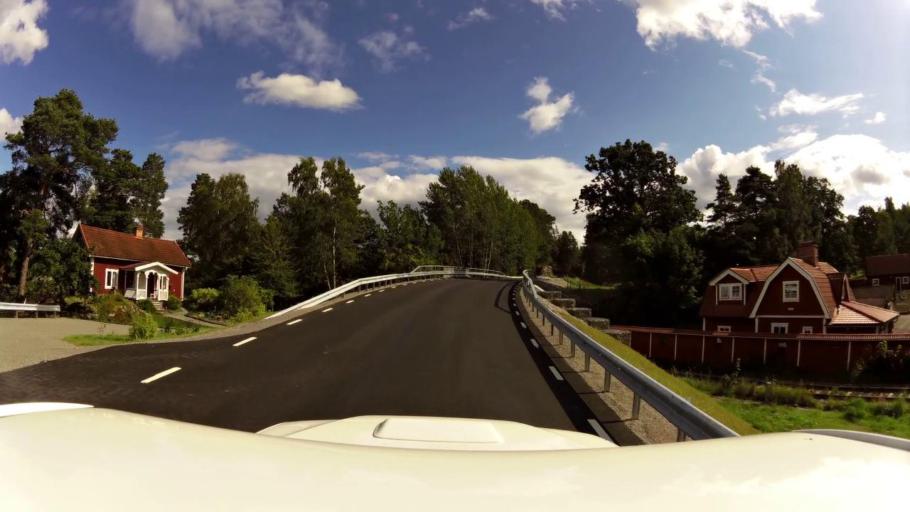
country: SE
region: OEstergoetland
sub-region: Kinda Kommun
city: Rimforsa
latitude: 58.2282
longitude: 15.7016
